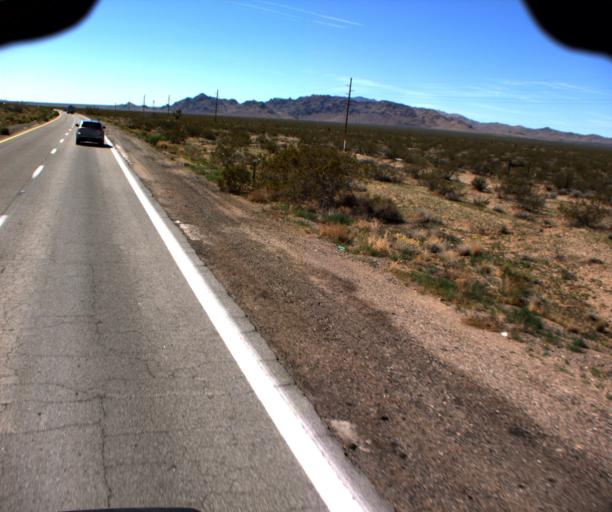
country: US
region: Arizona
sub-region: Mohave County
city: Dolan Springs
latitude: 35.6892
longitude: -114.4698
